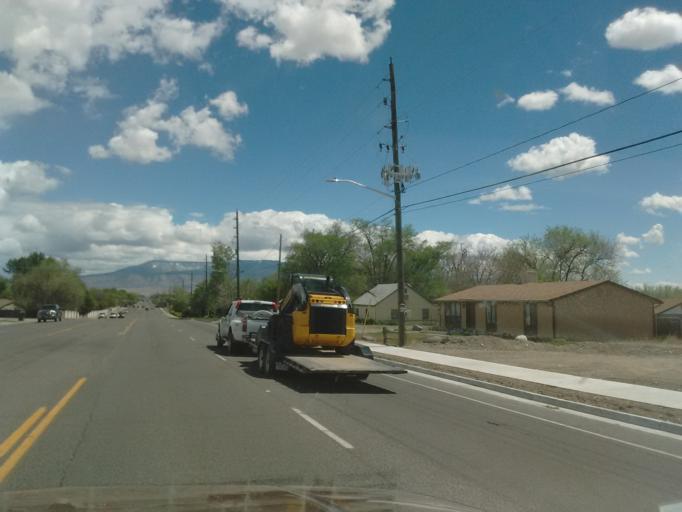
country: US
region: Colorado
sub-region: Mesa County
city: Fruitvale
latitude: 39.0918
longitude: -108.5212
